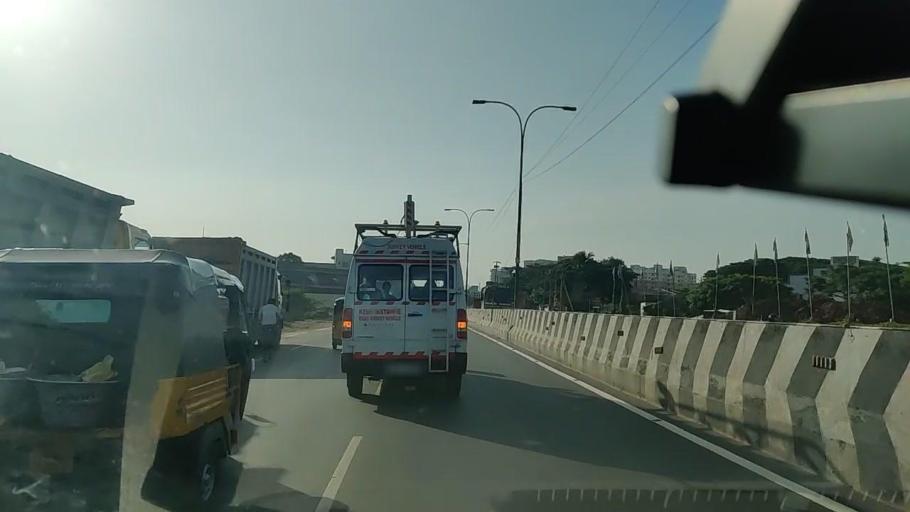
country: IN
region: Tamil Nadu
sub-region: Thiruvallur
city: Chinnasekkadu
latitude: 13.1418
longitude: 80.2240
